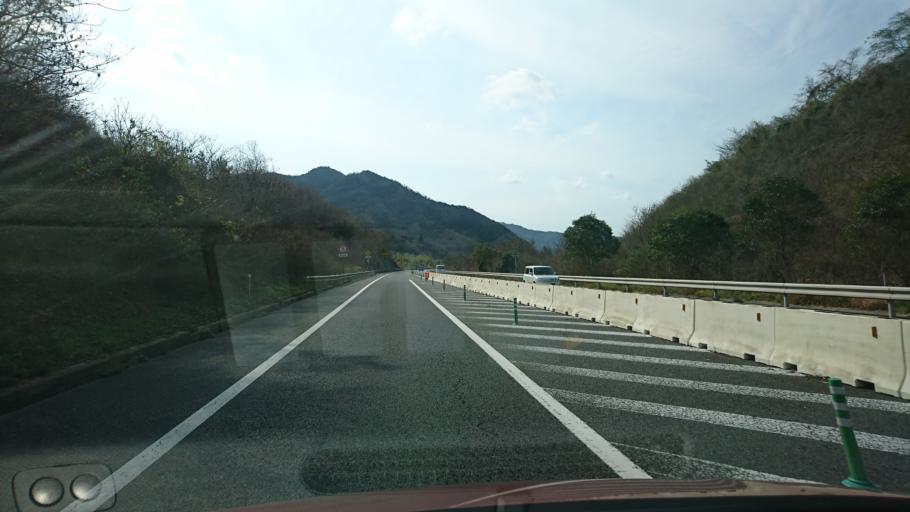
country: JP
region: Hiroshima
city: Innoshima
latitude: 34.1377
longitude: 133.0537
